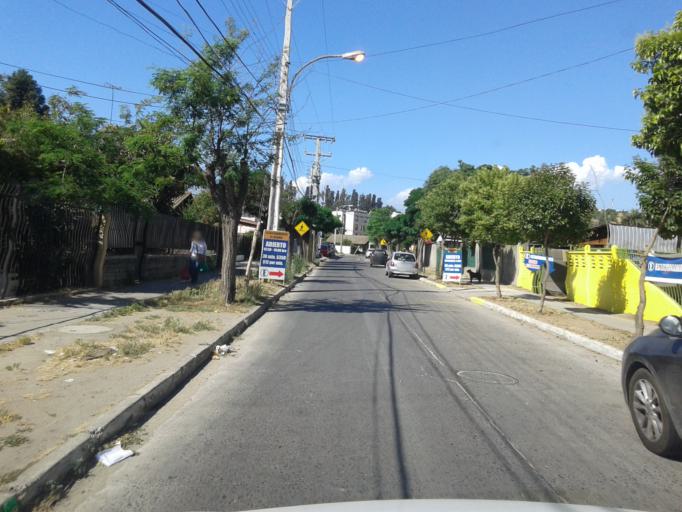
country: CL
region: Valparaiso
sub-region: Provincia de Quillota
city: Quillota
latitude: -32.8784
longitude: -71.2581
